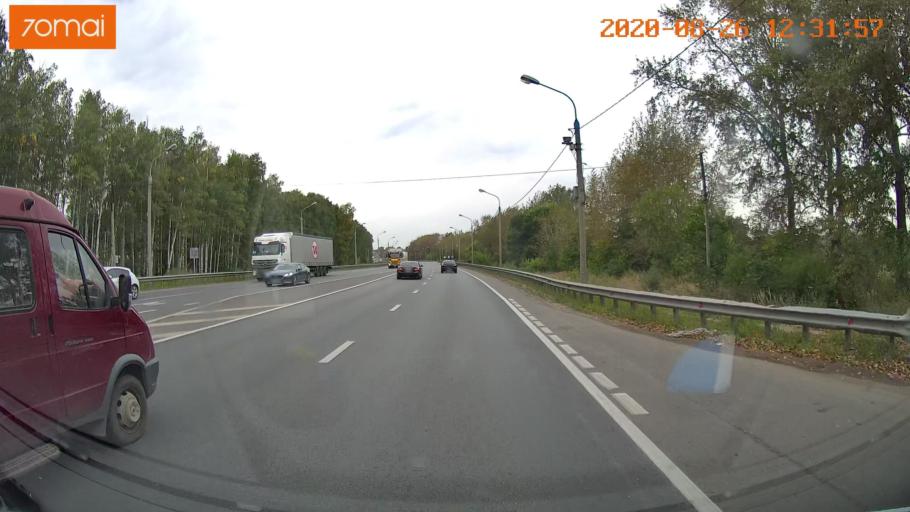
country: RU
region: Rjazan
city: Ryazan'
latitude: 54.5742
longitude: 39.7988
